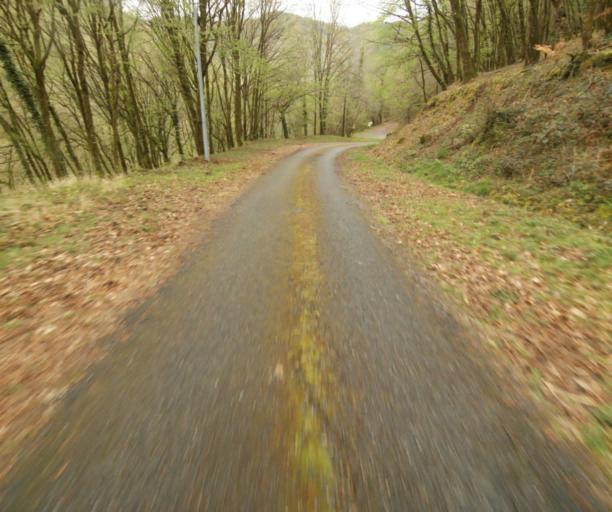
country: FR
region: Limousin
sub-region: Departement de la Correze
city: Saint-Privat
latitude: 45.2151
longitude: 2.0368
